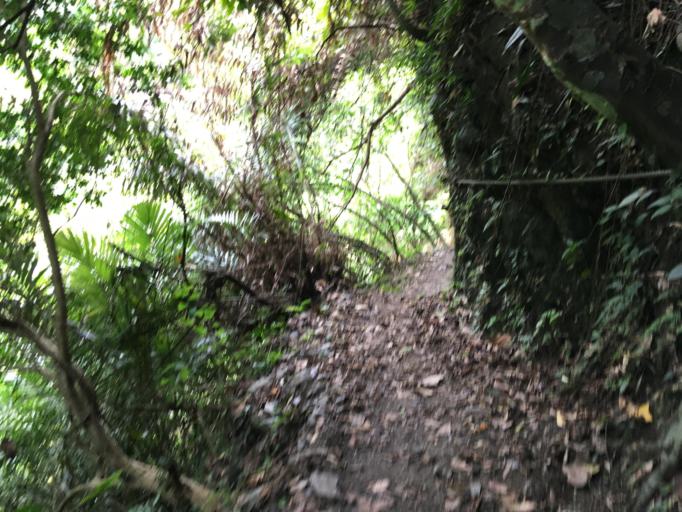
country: TW
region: Taiwan
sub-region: Yilan
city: Yilan
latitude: 24.4243
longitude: 121.7024
